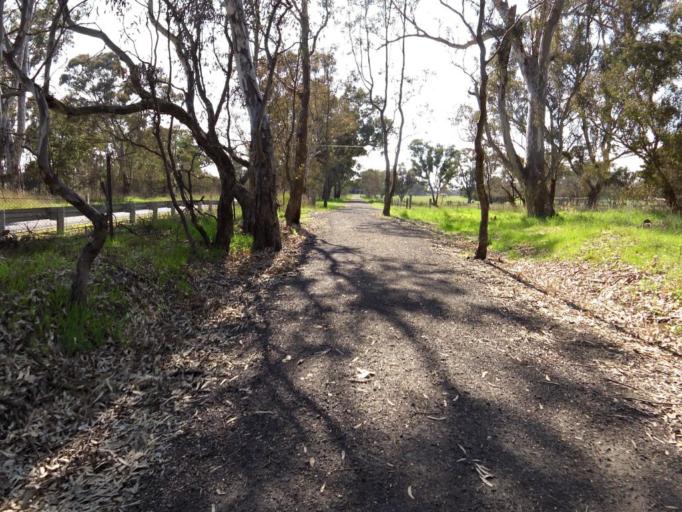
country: AU
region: Victoria
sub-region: Murrindindi
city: Alexandra
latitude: -37.1159
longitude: 145.6062
